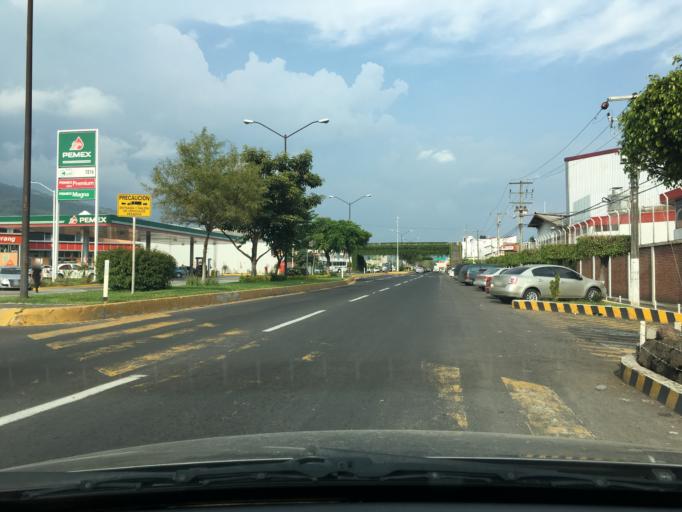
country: MX
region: Michoacan
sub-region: Uruapan
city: Uruapan
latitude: 19.4184
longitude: -102.0456
